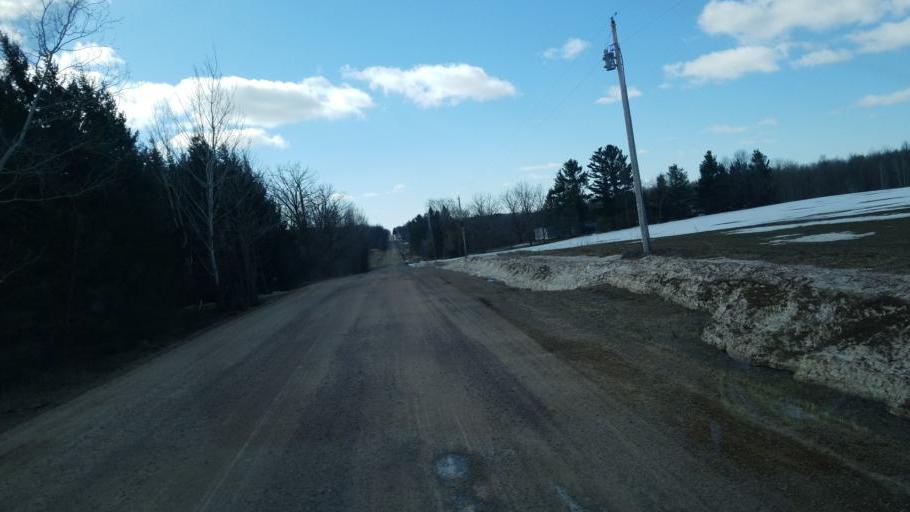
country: US
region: Wisconsin
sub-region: Clark County
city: Loyal
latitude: 44.6811
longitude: -90.4558
